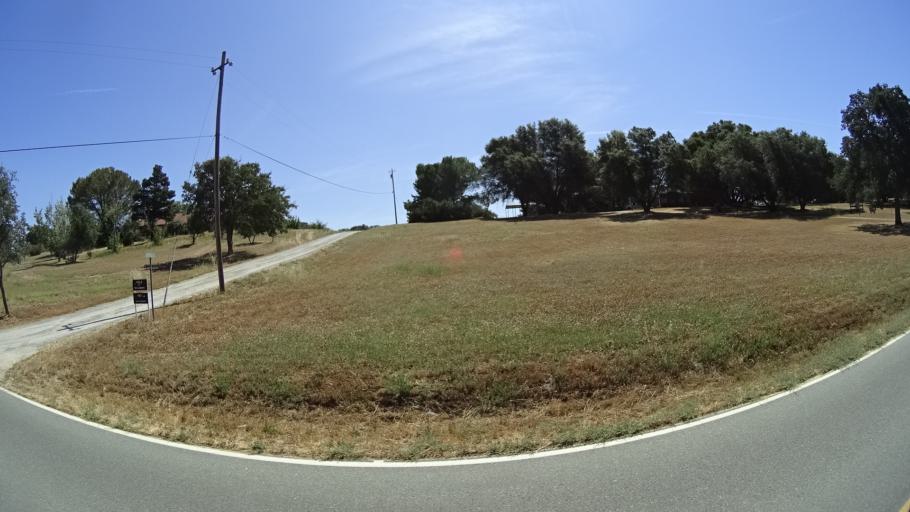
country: US
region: California
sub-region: Calaveras County
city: Rancho Calaveras
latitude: 38.1689
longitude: -120.9089
